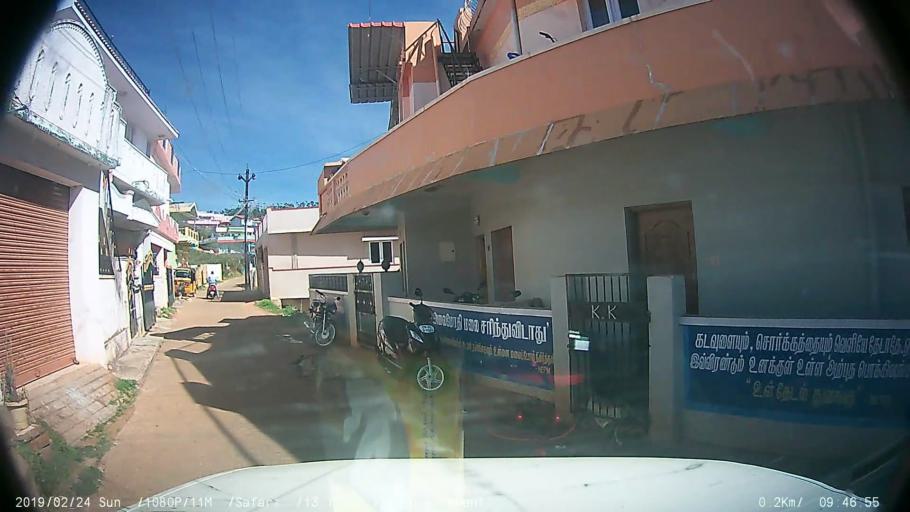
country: IN
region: Tamil Nadu
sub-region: Nilgiri
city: Wellington
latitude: 11.3470
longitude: 76.7797
